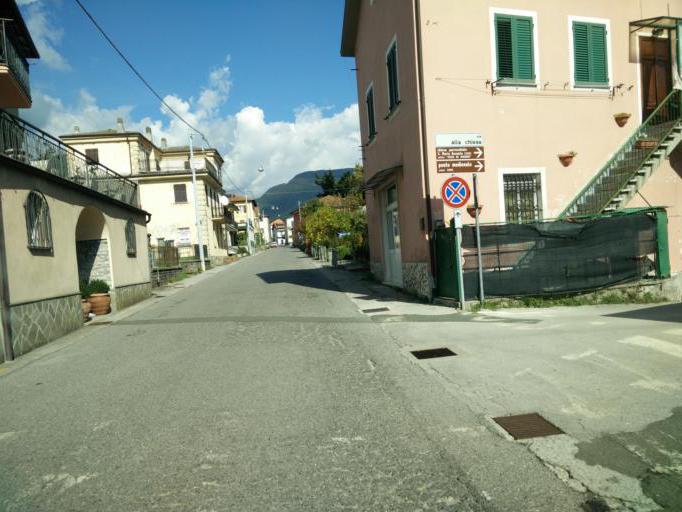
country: IT
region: Liguria
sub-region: Provincia di La Spezia
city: Sesta Godano
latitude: 44.2906
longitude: 9.6724
